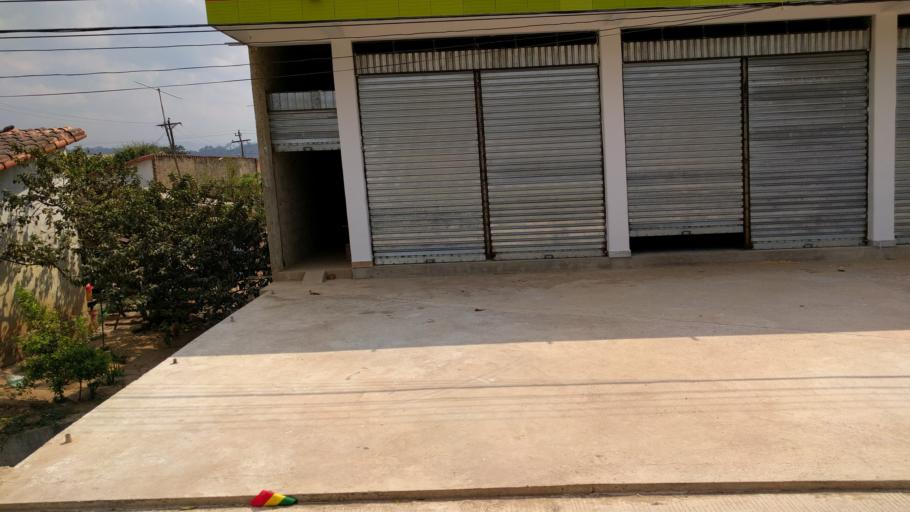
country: BO
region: Santa Cruz
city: Santiago del Torno
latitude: -18.0017
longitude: -63.3881
